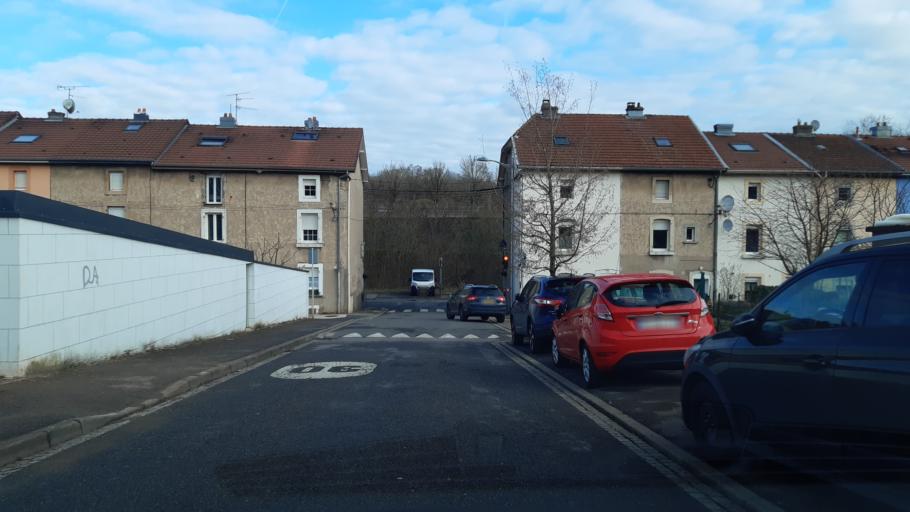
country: FR
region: Lorraine
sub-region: Departement de Meurthe-et-Moselle
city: Villerupt
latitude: 49.4742
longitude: 5.9393
